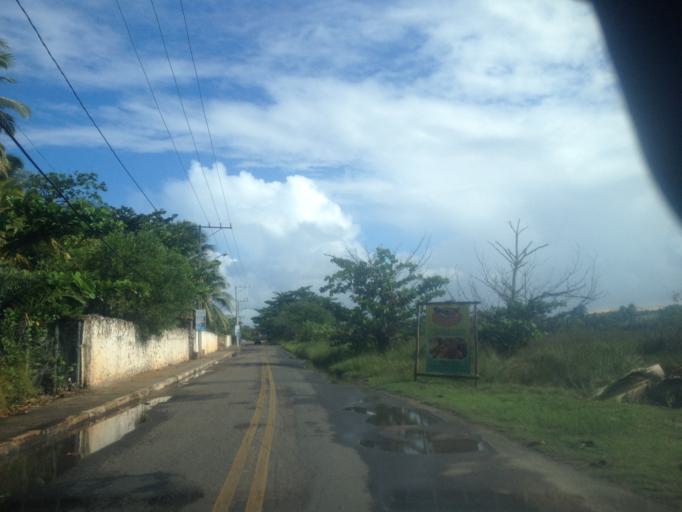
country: BR
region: Bahia
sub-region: Mata De Sao Joao
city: Mata de Sao Joao
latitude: -12.6098
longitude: -38.0424
